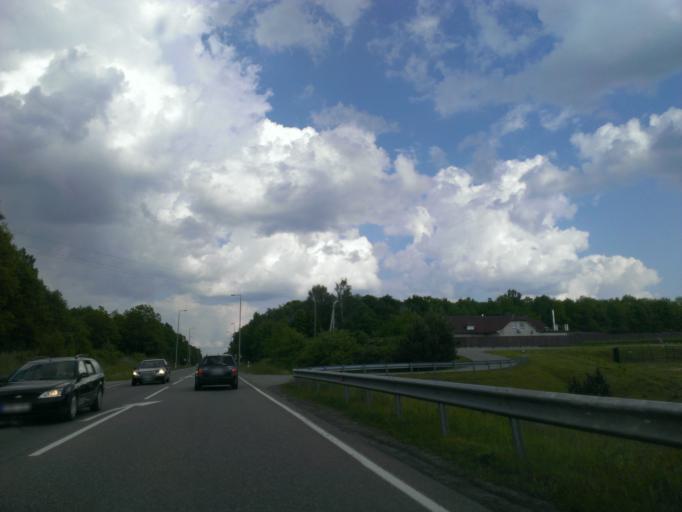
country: LT
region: Klaipedos apskritis
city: Kretinga
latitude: 55.8955
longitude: 21.1970
